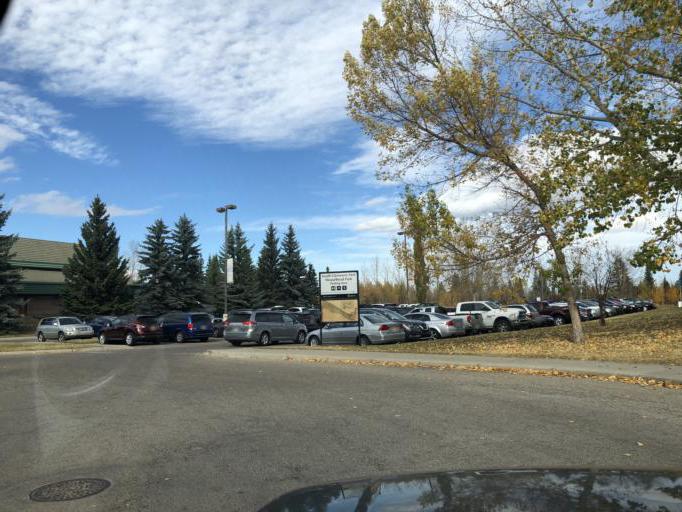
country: CA
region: Alberta
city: Calgary
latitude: 50.9770
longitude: -114.1356
